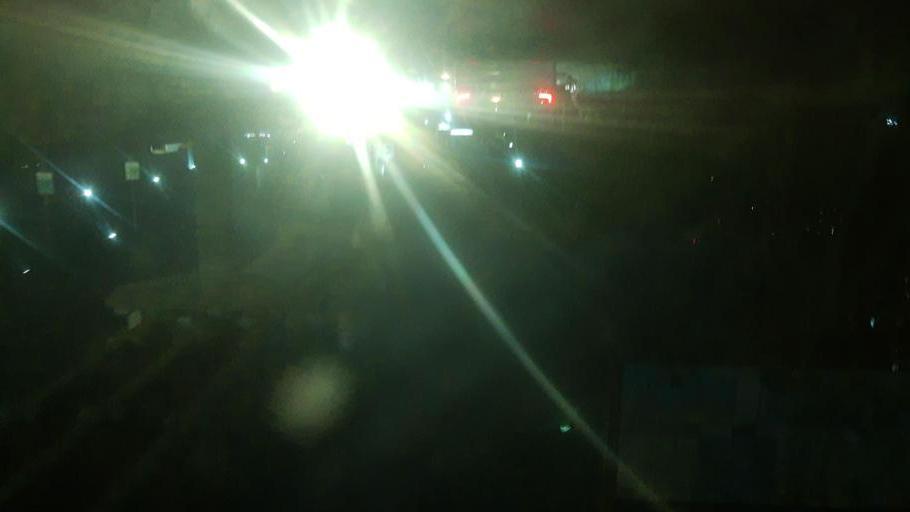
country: IN
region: Maharashtra
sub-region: Thane
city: Thane
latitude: 19.2105
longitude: 72.9744
